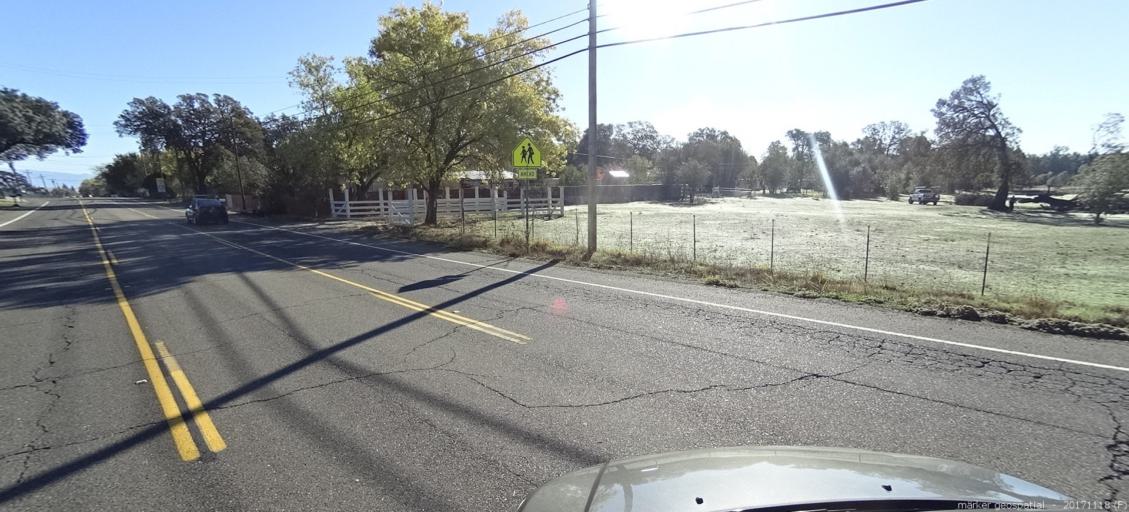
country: US
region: California
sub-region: Shasta County
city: Cottonwood
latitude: 40.3893
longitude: -122.3179
